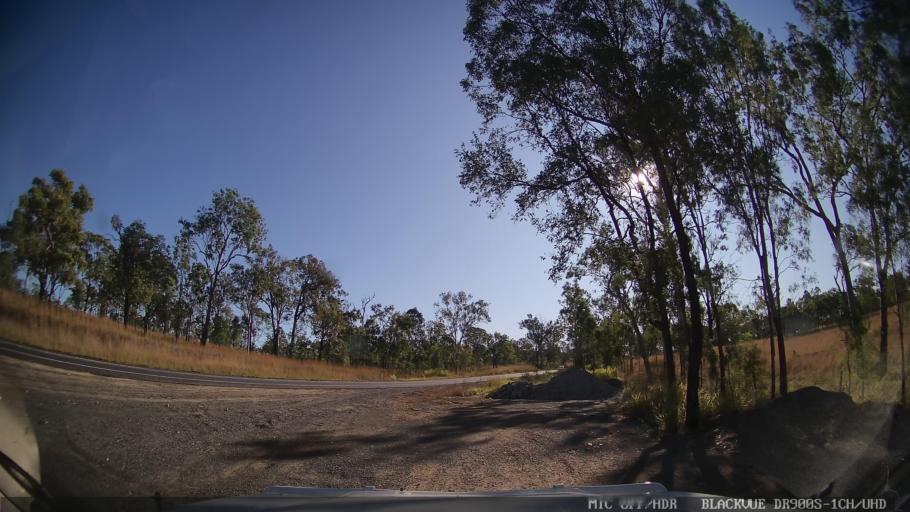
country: AU
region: Queensland
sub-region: Bundaberg
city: Sharon
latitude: -24.8781
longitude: 151.7432
